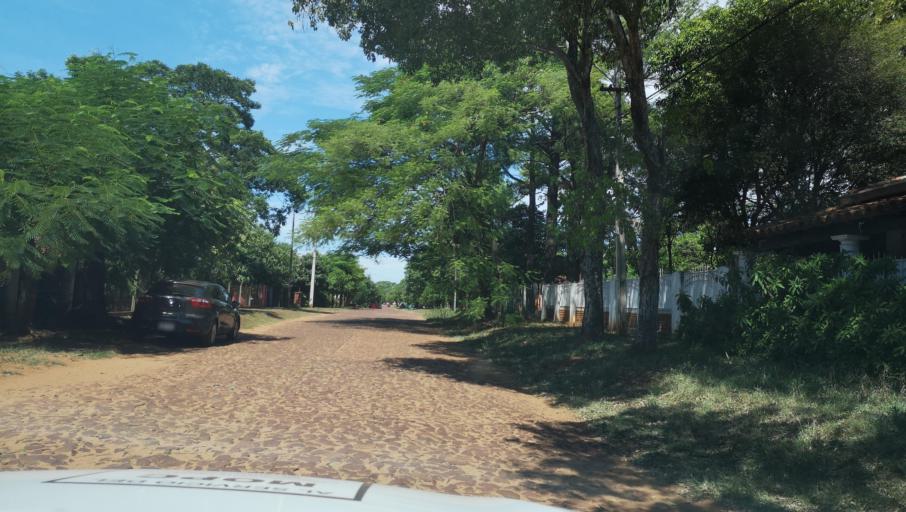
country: PY
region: Misiones
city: Santa Maria
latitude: -26.8941
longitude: -57.0285
